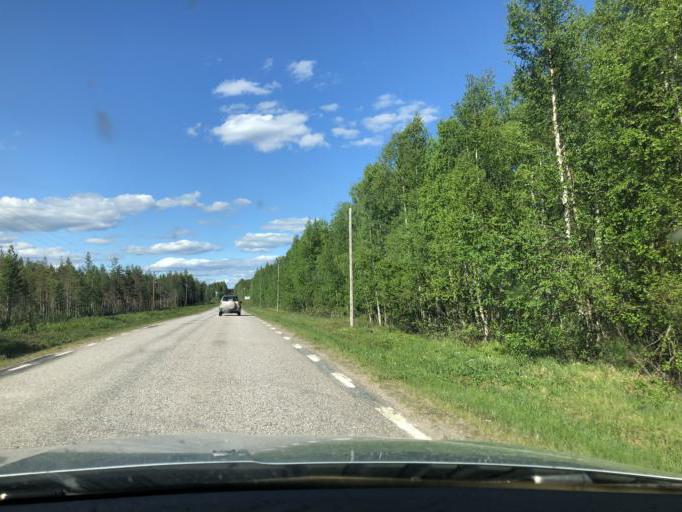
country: SE
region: Norrbotten
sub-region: Kalix Kommun
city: Kalix
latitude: 66.0524
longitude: 23.1888
